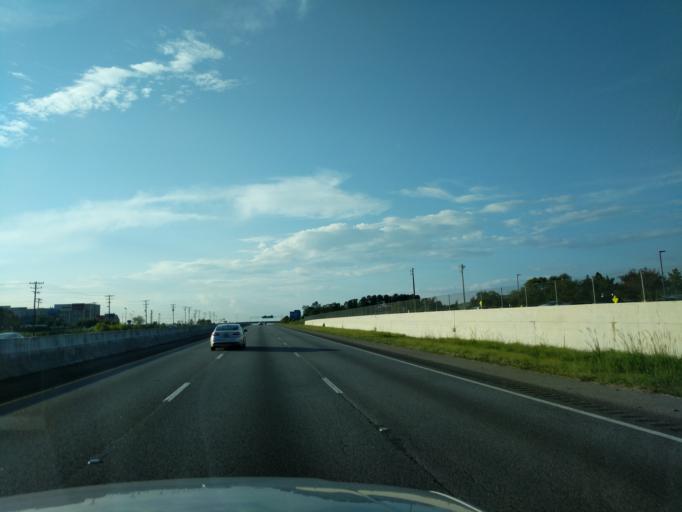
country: US
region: South Carolina
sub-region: Greenville County
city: Simpsonville
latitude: 34.7131
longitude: -82.2486
